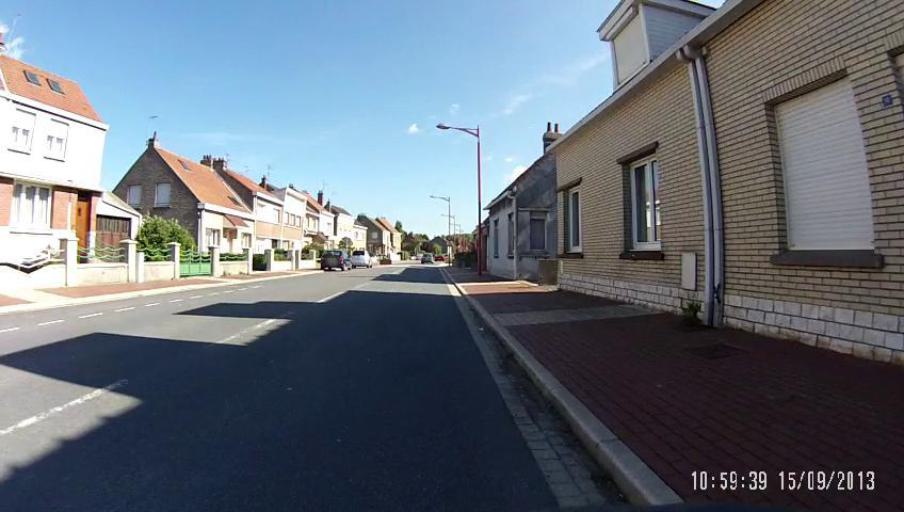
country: FR
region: Nord-Pas-de-Calais
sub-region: Departement du Nord
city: Zuydcoote
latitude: 51.0646
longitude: 2.4908
